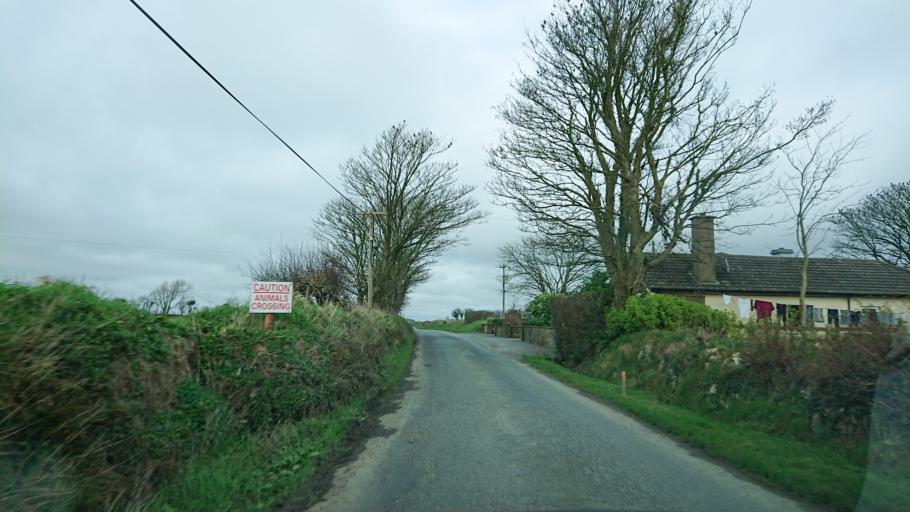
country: IE
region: Munster
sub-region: Waterford
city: Portlaw
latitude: 52.1759
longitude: -7.3038
